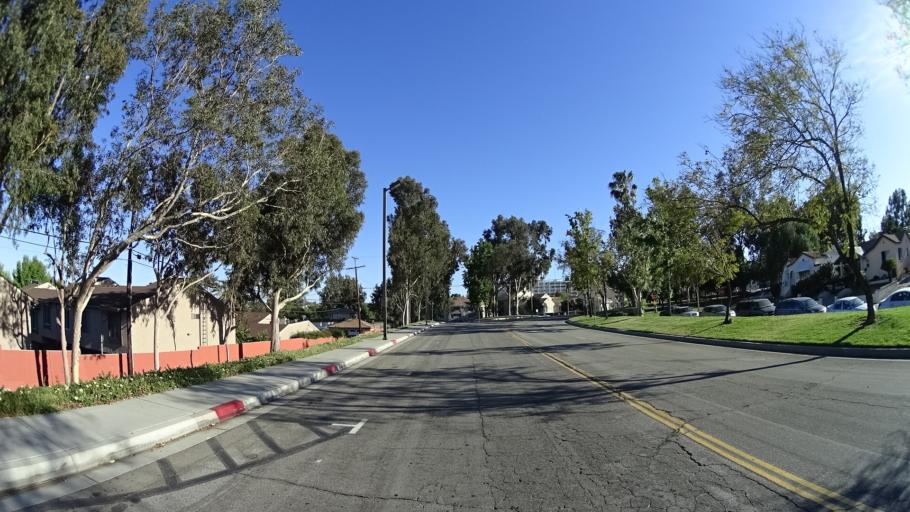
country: US
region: California
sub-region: Los Angeles County
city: Belvedere
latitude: 34.0725
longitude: -118.1651
